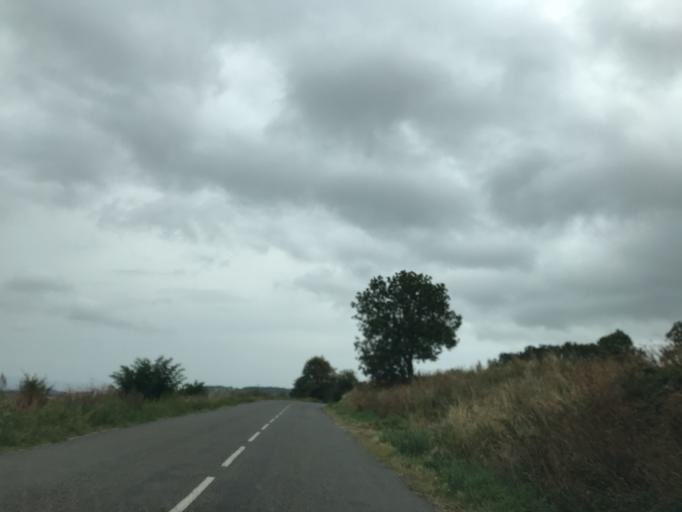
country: FR
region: Rhone-Alpes
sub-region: Departement de la Loire
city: Sail-sous-Couzan
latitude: 45.6780
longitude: 3.8969
